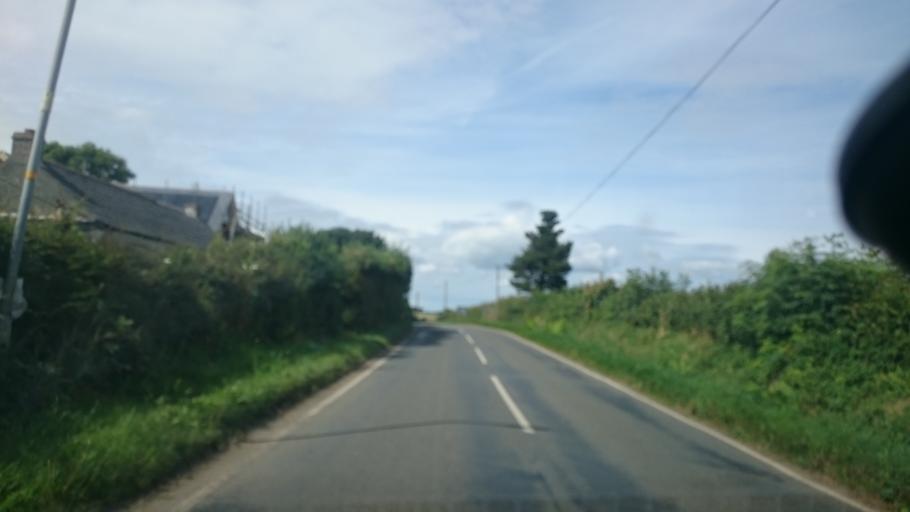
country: GB
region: Wales
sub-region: Pembrokeshire
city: Freystrop
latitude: 51.7528
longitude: -4.9535
